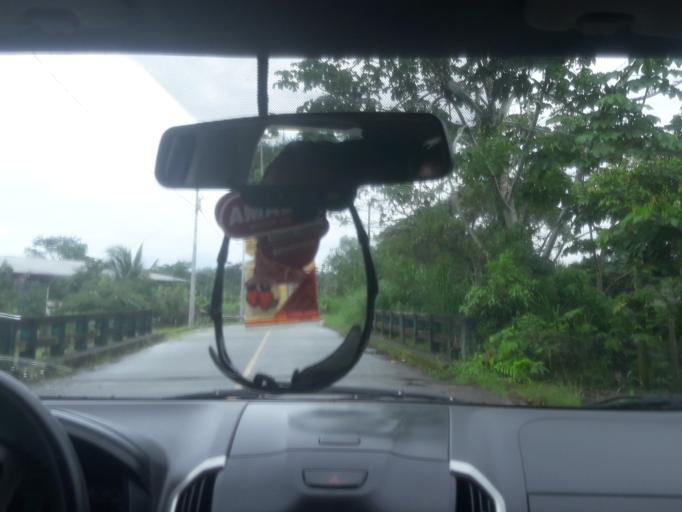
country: EC
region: Napo
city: Tena
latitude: -1.0412
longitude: -77.6965
